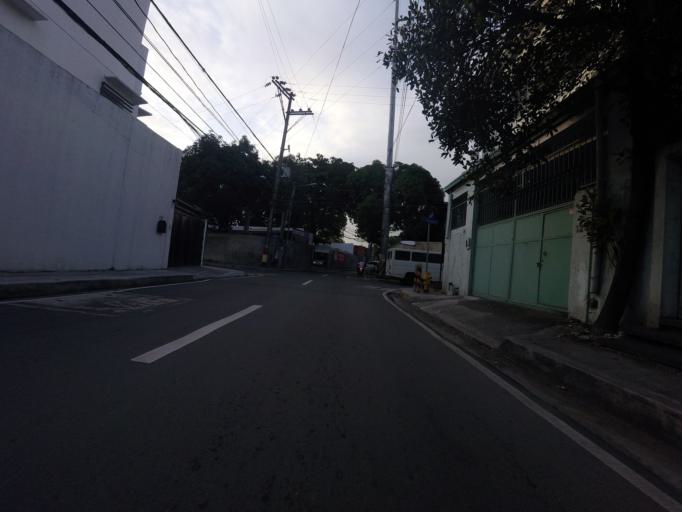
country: PH
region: Metro Manila
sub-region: San Juan
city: San Juan
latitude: 14.5926
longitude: 121.0332
